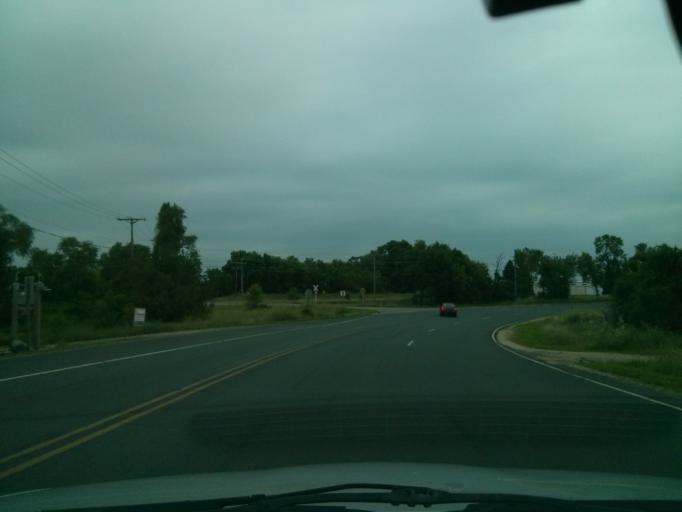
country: US
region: Wisconsin
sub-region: Saint Croix County
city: North Hudson
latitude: 44.9908
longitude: -92.7059
